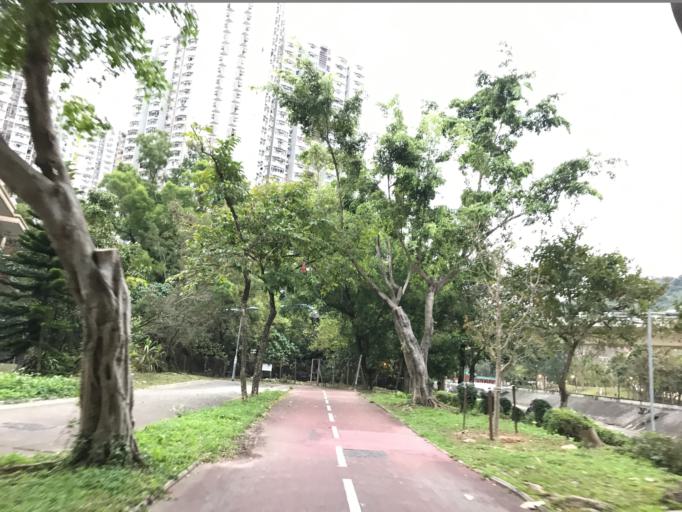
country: HK
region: Tai Po
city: Tai Po
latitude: 22.4511
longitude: 114.1573
